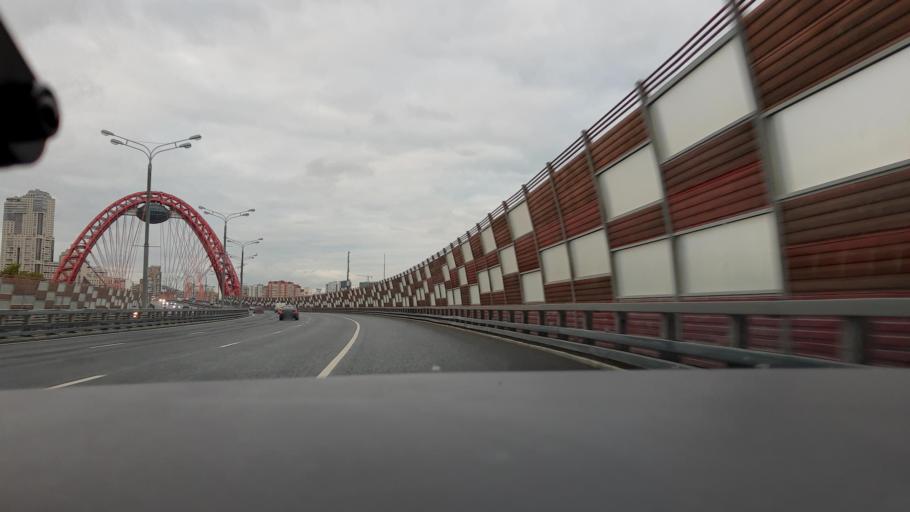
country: RU
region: Moscow
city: Shchukino
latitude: 55.7720
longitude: 37.4363
